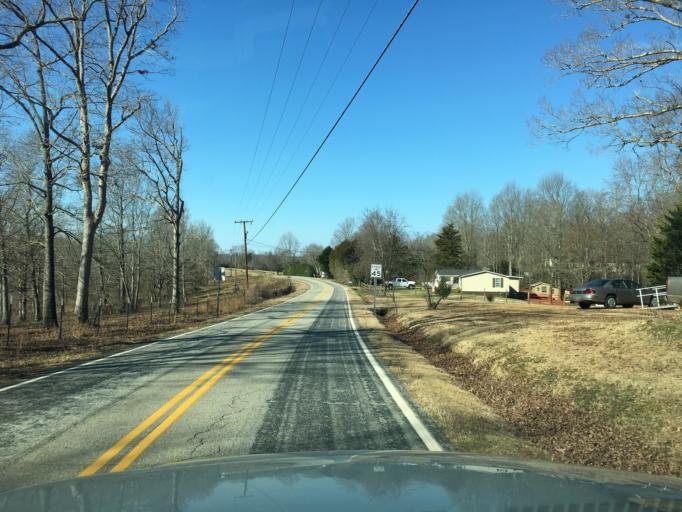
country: US
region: South Carolina
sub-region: Pickens County
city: Pickens
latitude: 34.8715
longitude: -82.7290
